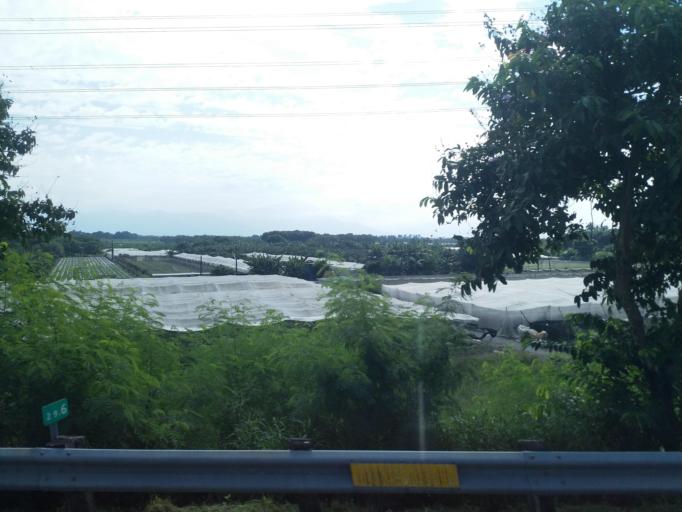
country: TW
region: Taiwan
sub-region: Pingtung
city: Pingtung
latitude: 22.8338
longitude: 120.4929
